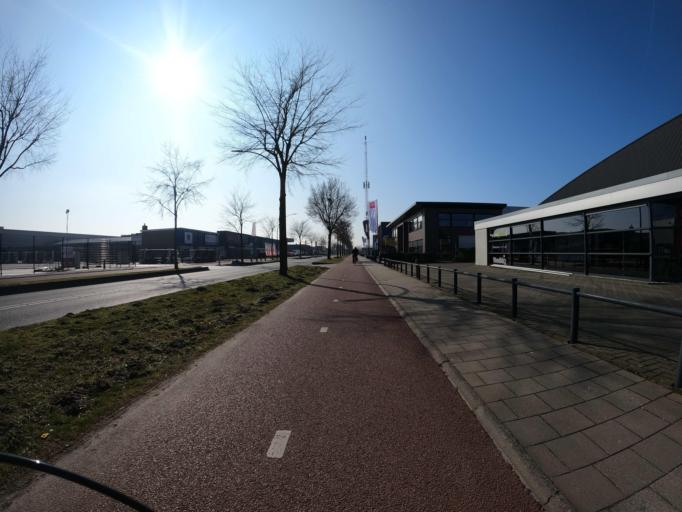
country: NL
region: Gelderland
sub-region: Gemeente Harderwijk
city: Harderwijk
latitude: 52.3584
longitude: 5.6365
